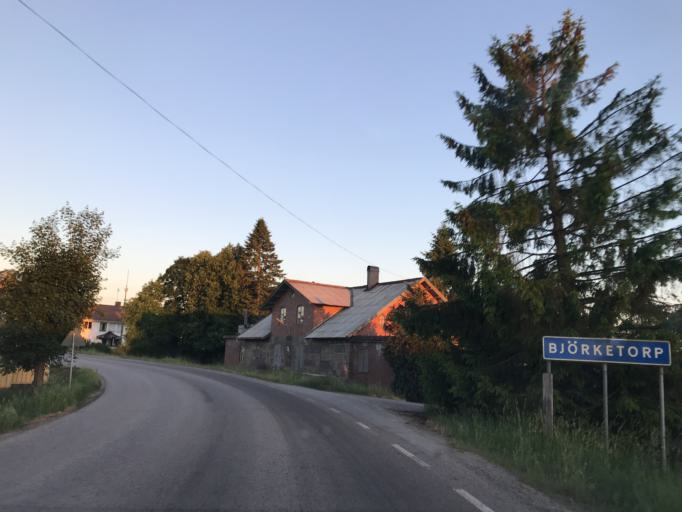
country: SE
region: Vaestra Goetaland
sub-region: Marks Kommun
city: Horred
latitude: 57.4262
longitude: 12.5205
